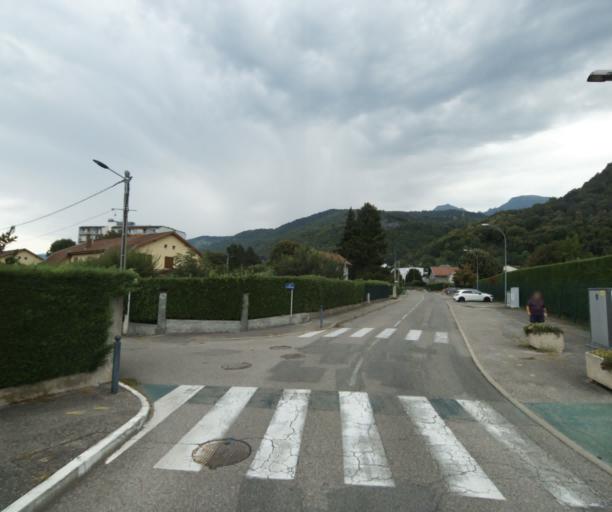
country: FR
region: Rhone-Alpes
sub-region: Departement de l'Isere
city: Domene
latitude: 45.2018
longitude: 5.8336
